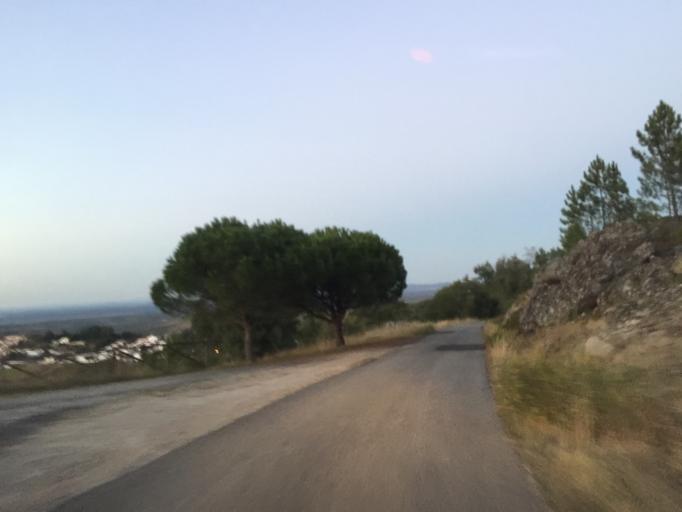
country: PT
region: Portalegre
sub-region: Castelo de Vide
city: Castelo de Vide
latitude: 39.4029
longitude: -7.4494
